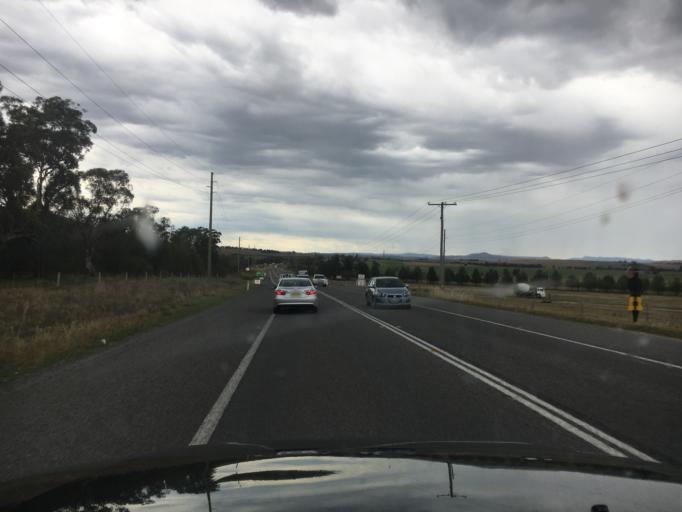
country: AU
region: New South Wales
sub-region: Muswellbrook
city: Muswellbrook
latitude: -32.1819
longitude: 150.8903
